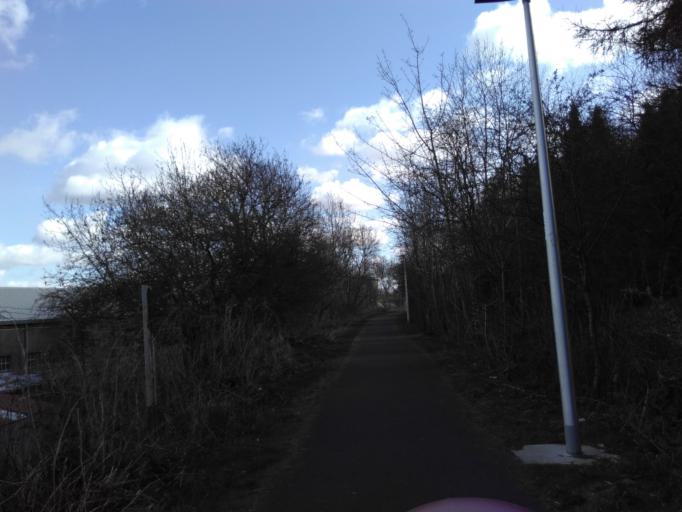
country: GB
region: Scotland
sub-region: Midlothian
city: Loanhead
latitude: 55.8824
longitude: -3.1445
